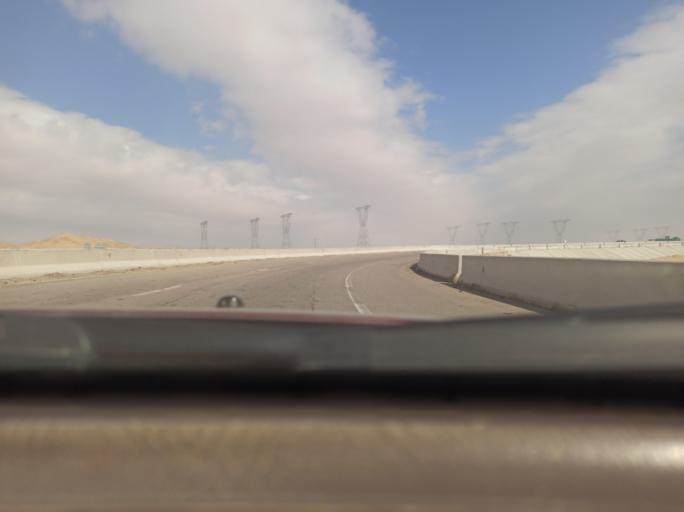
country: EG
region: Muhafazat al Fayyum
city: Tamiyah
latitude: 29.6438
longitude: 31.0118
